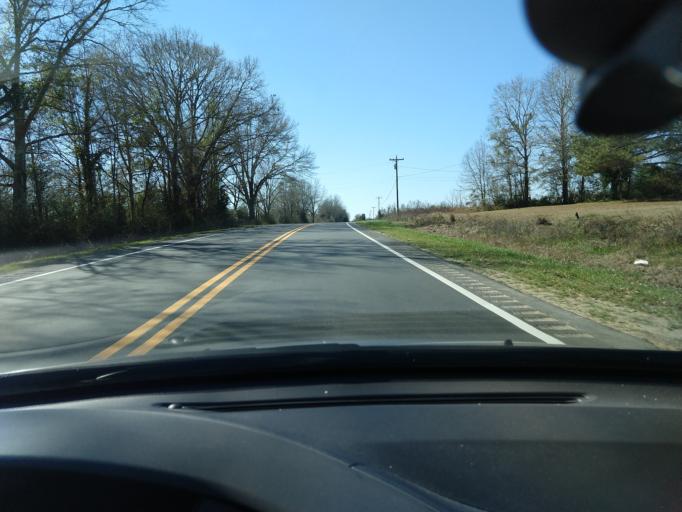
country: US
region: Alabama
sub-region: Covington County
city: Andalusia
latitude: 31.2532
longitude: -86.5199
